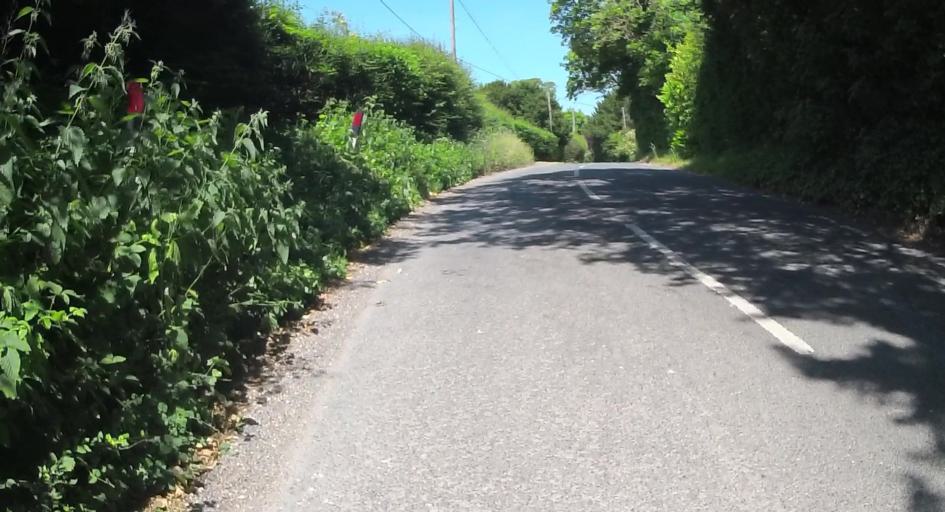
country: GB
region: England
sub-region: Hampshire
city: Tadley
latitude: 51.3018
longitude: -1.1278
